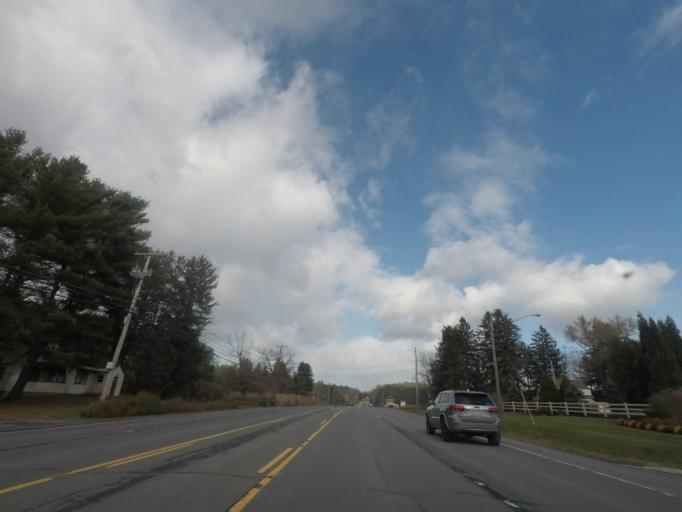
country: US
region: New York
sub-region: Saratoga County
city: Ballston Spa
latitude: 43.0017
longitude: -73.7907
